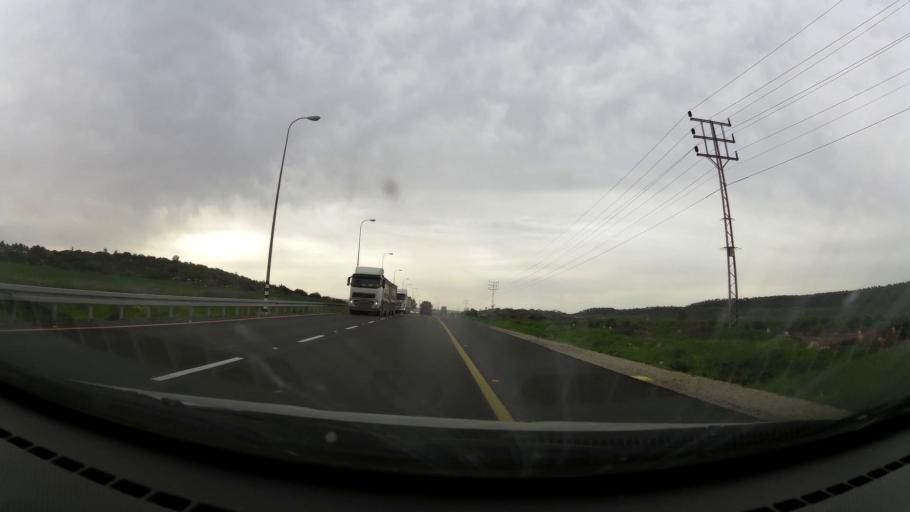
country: IL
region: Jerusalem
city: Bet Shemesh
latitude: 31.6779
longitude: 35.0047
